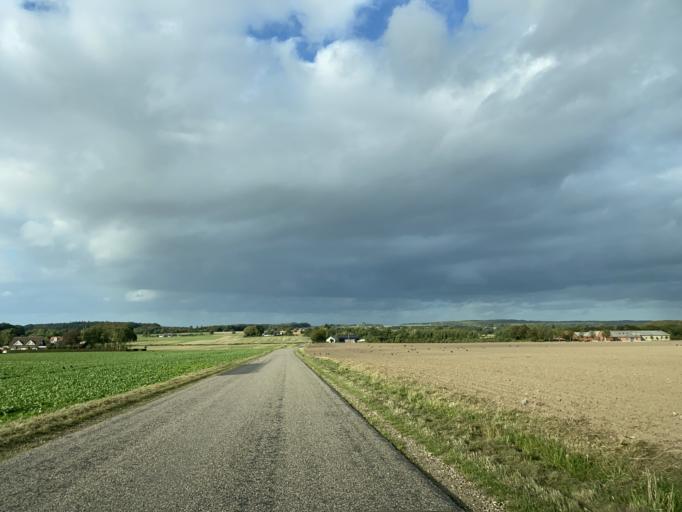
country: DK
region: Central Jutland
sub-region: Skanderborg Kommune
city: Galten
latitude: 56.1561
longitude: 9.8391
